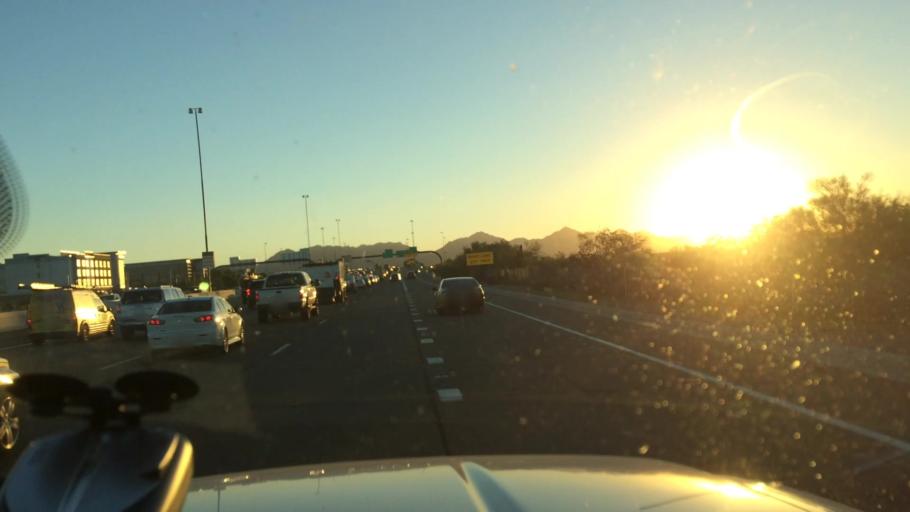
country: US
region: Arizona
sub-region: Maricopa County
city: Paradise Valley
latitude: 33.6726
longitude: -111.9862
